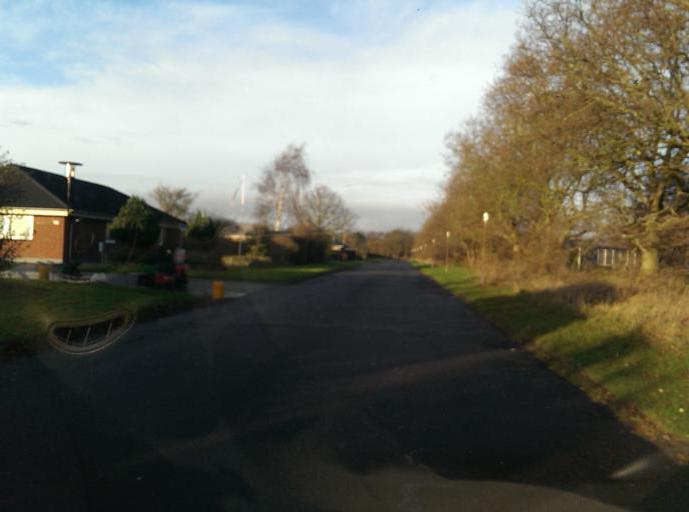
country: DK
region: South Denmark
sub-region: Esbjerg Kommune
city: Tjaereborg
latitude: 55.4616
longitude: 8.5926
